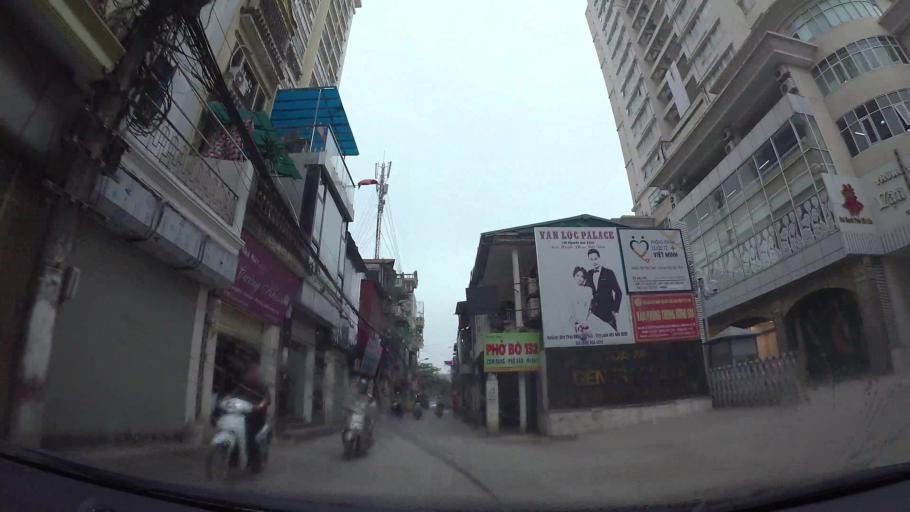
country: VN
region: Ha Noi
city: Hai BaTrung
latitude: 20.9871
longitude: 105.8519
